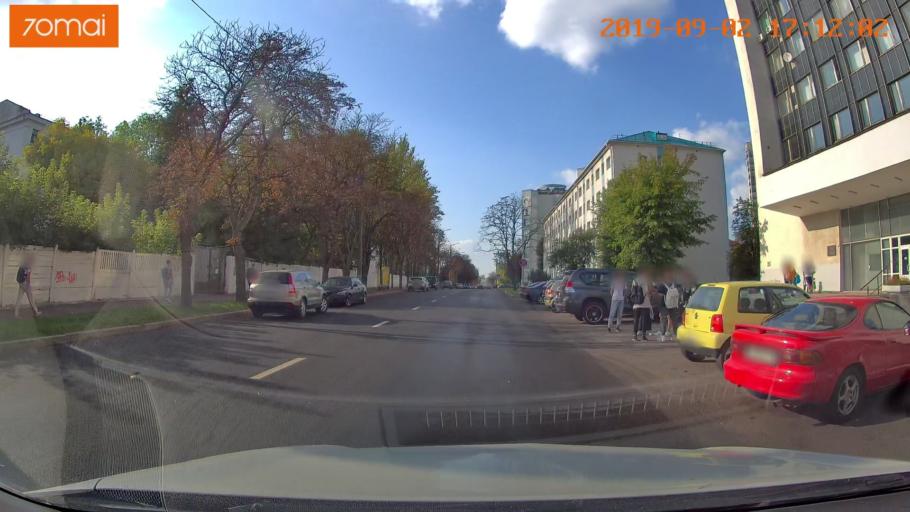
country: BY
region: Minsk
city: Minsk
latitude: 53.9162
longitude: 27.6021
